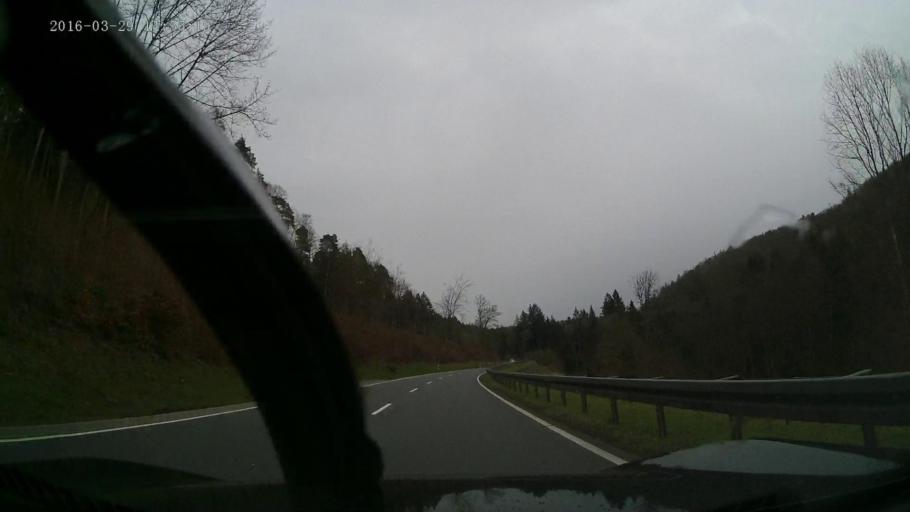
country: DE
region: Baden-Wuerttemberg
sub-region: Karlsruhe Region
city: Walldurn
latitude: 49.6090
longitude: 9.3340
